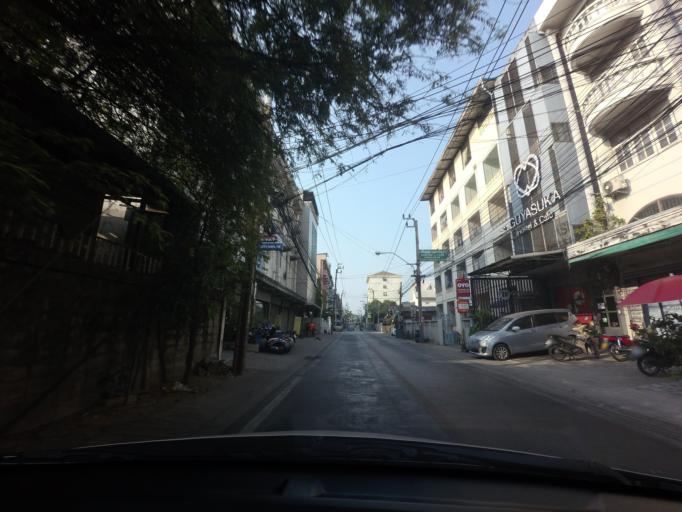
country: TH
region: Bangkok
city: Bang Na
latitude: 13.6605
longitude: 100.6121
